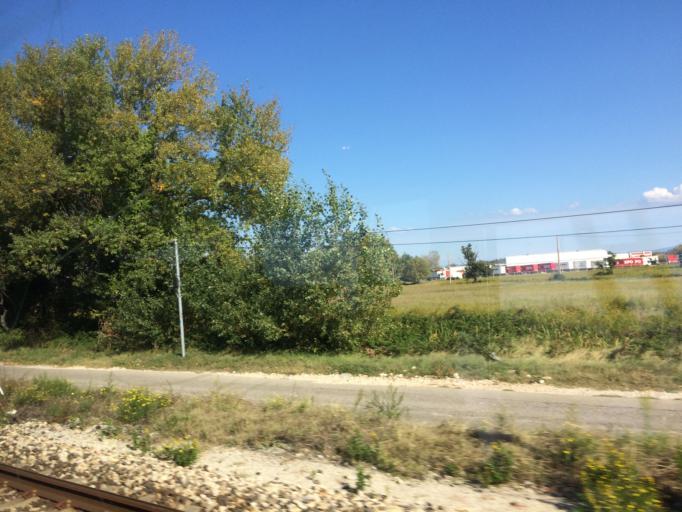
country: FR
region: Provence-Alpes-Cote d'Azur
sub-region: Departement du Vaucluse
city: Le Pontet
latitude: 43.9773
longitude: 4.8636
